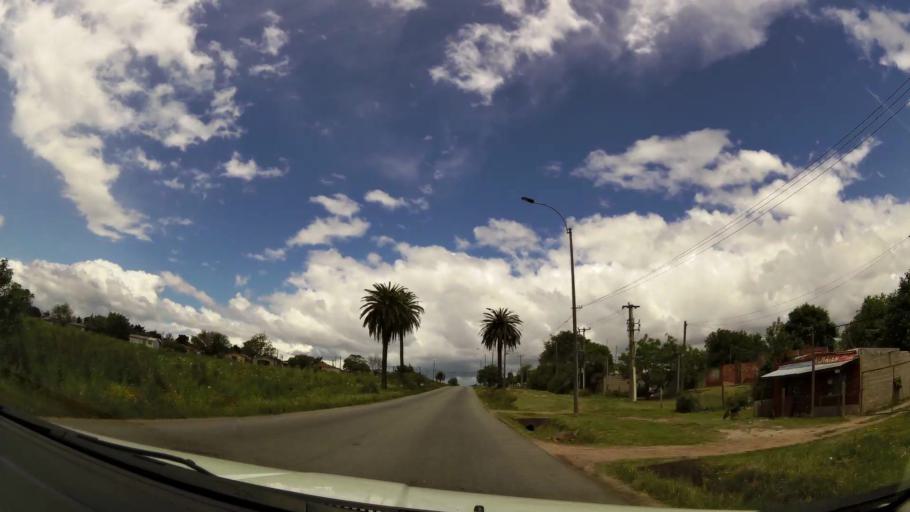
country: UY
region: Canelones
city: La Paz
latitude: -34.8167
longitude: -56.1683
